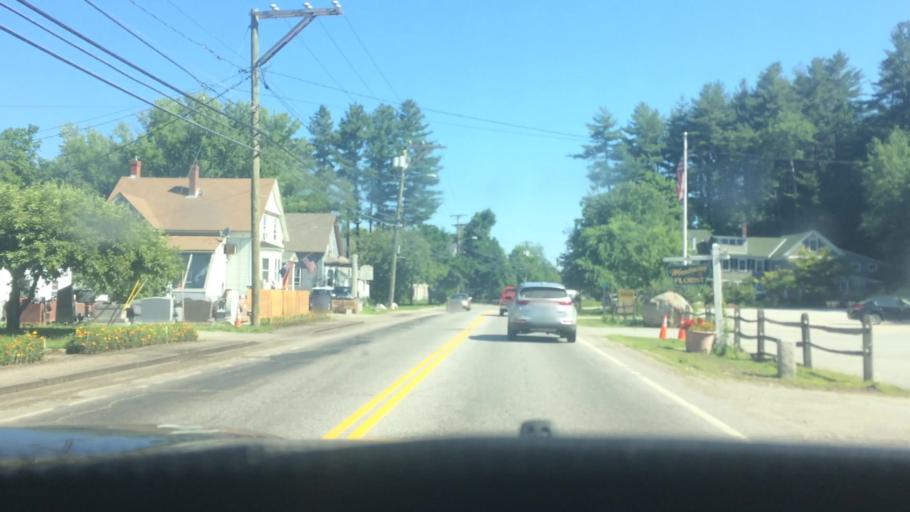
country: US
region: New Hampshire
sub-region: Hillsborough County
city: Peterborough
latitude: 42.8834
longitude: -71.9463
